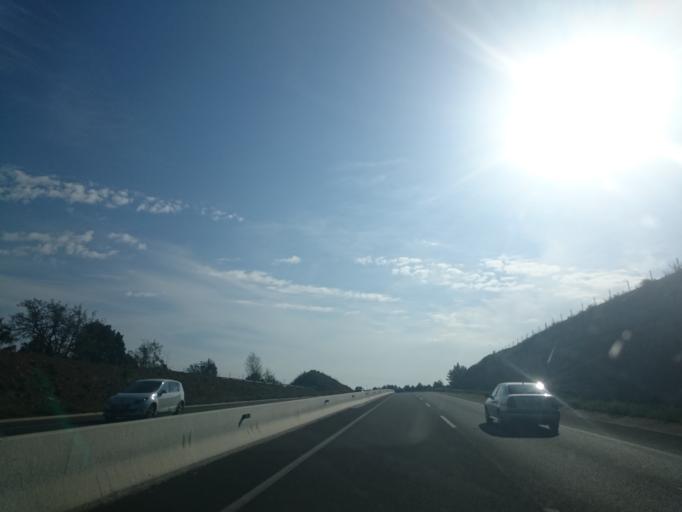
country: ES
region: Catalonia
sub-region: Provincia de Barcelona
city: Santa Maria d'Olo
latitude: 41.8842
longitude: 2.0384
